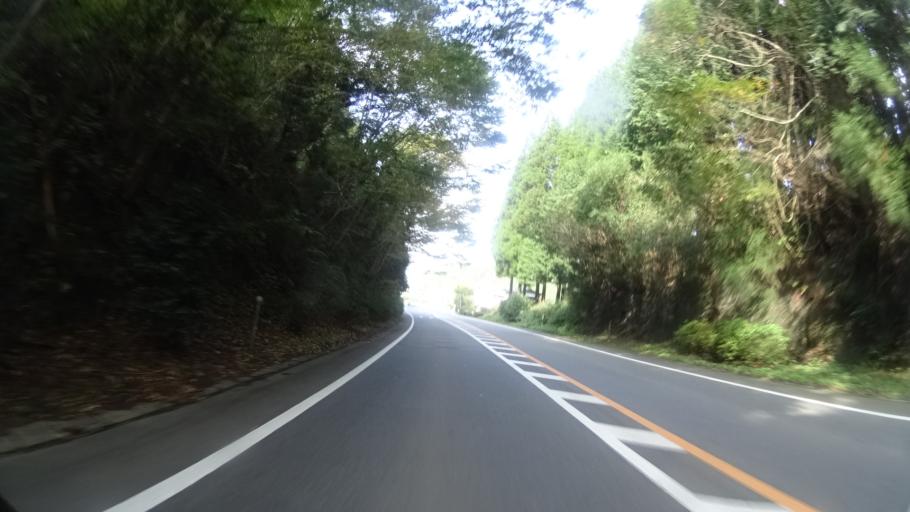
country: JP
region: Kumamoto
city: Aso
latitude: 33.0876
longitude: 131.0677
